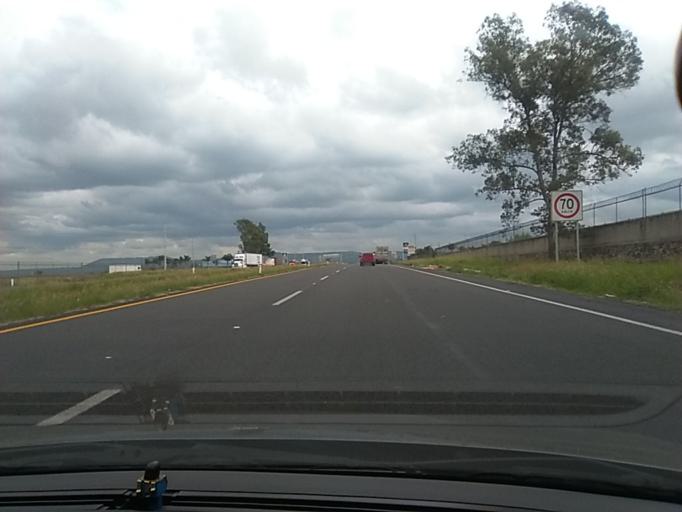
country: MX
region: Jalisco
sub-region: Tonala
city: Mismaloya (Fraccionamiento Pedregal de Santa Martha)
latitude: 20.6056
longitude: -103.1316
